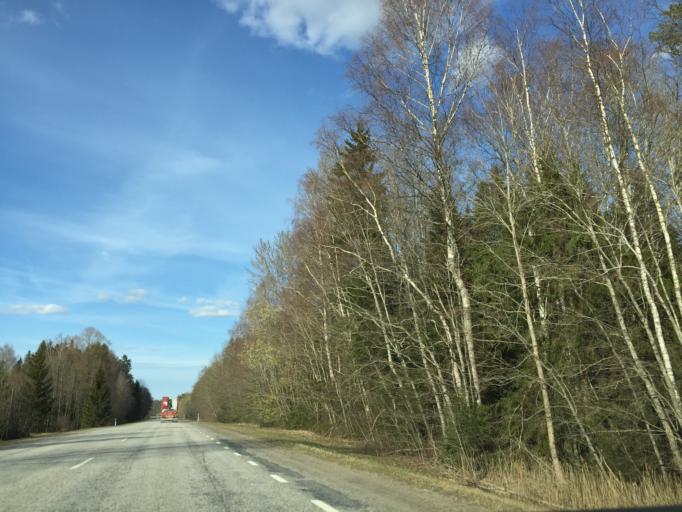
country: EE
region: Tartu
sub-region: Elva linn
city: Elva
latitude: 58.1182
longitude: 26.5144
